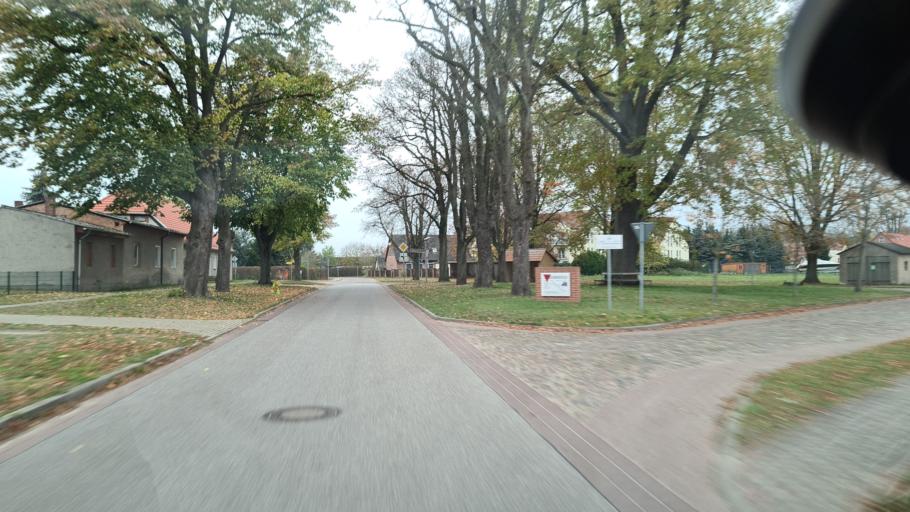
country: DE
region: Brandenburg
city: Lindow
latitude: 52.9323
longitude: 13.0153
